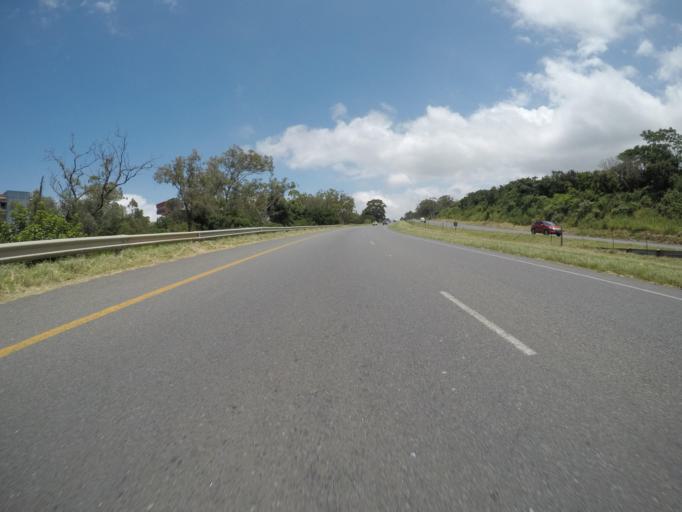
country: ZA
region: Eastern Cape
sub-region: Buffalo City Metropolitan Municipality
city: East London
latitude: -32.9466
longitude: 27.9405
